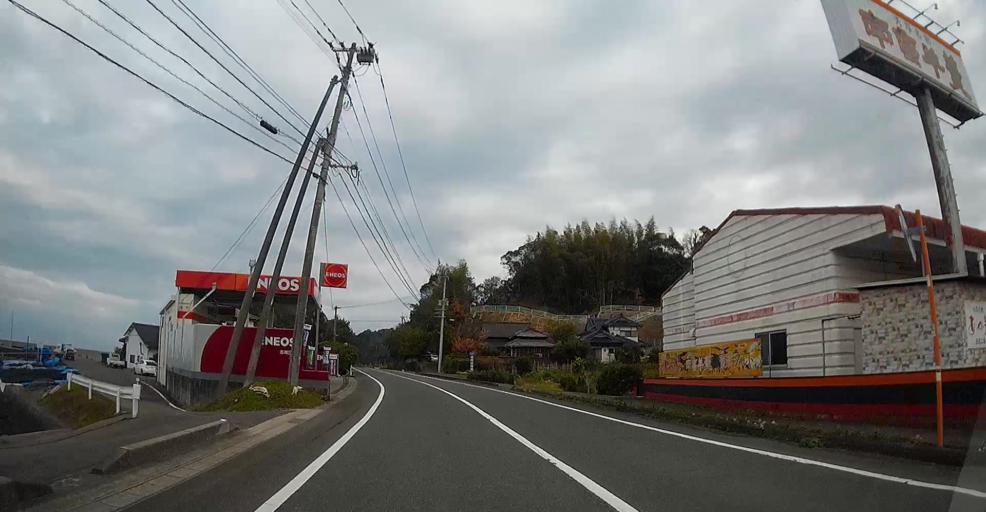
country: JP
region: Kumamoto
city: Hondo
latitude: 32.4613
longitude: 130.2359
